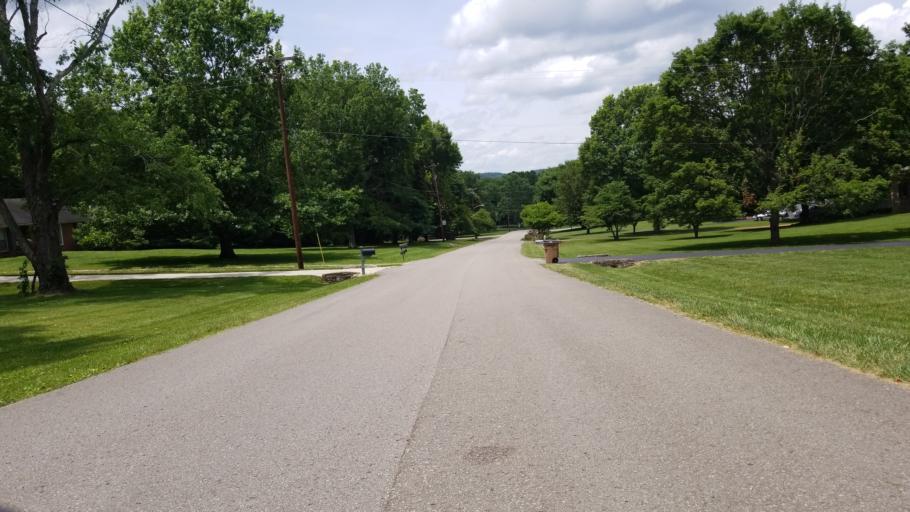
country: US
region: Tennessee
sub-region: Davidson County
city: Forest Hills
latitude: 36.0377
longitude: -86.8570
